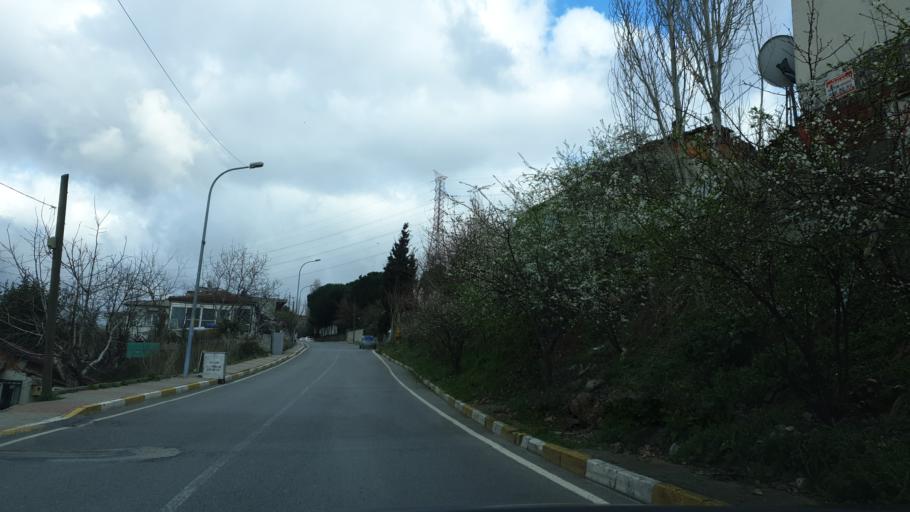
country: TR
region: Istanbul
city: Pendik
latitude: 40.8987
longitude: 29.2392
